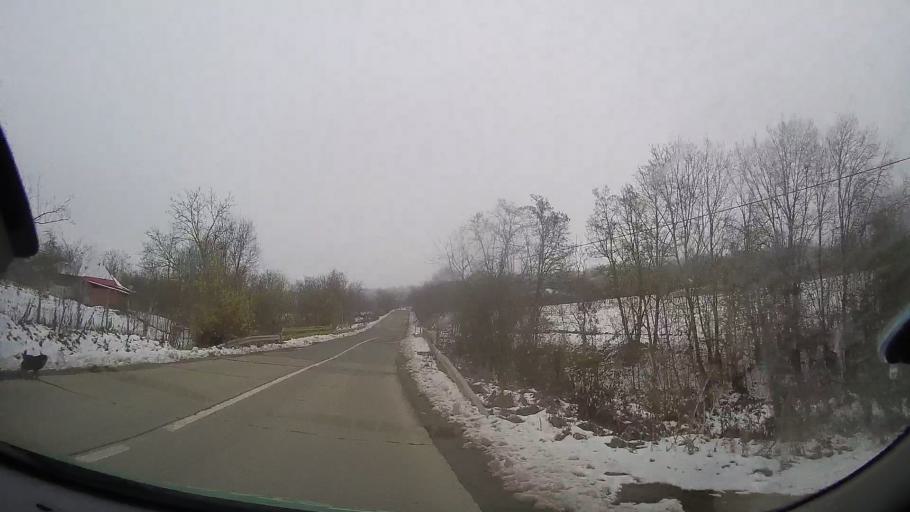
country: RO
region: Vrancea
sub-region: Comuna Boghesti
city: Boghesti
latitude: 46.2041
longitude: 27.4407
